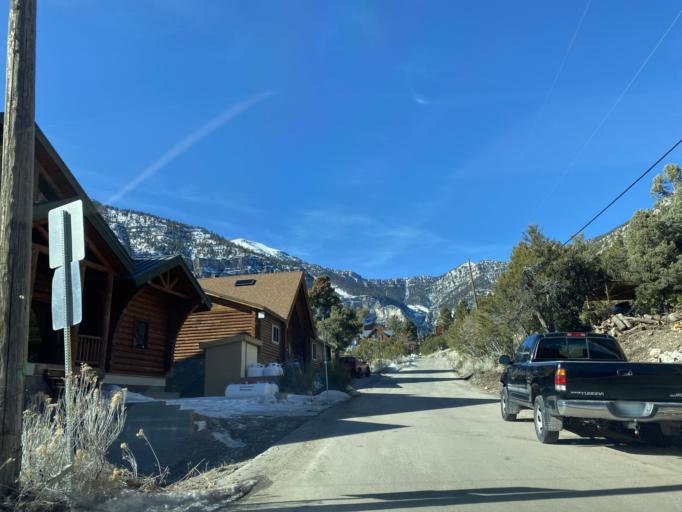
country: US
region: Nevada
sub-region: Nye County
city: Pahrump
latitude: 36.2632
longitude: -115.6527
